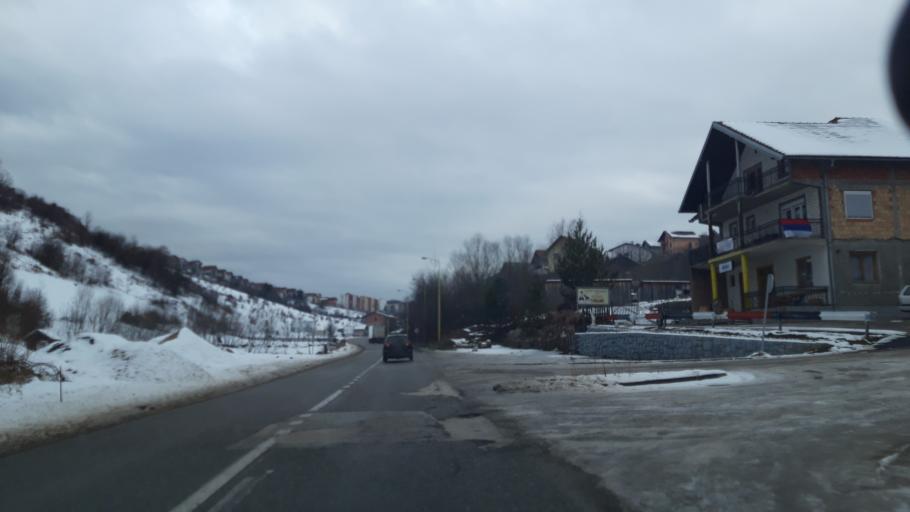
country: BA
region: Republika Srpska
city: Vlasenica
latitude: 44.1798
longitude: 18.9546
